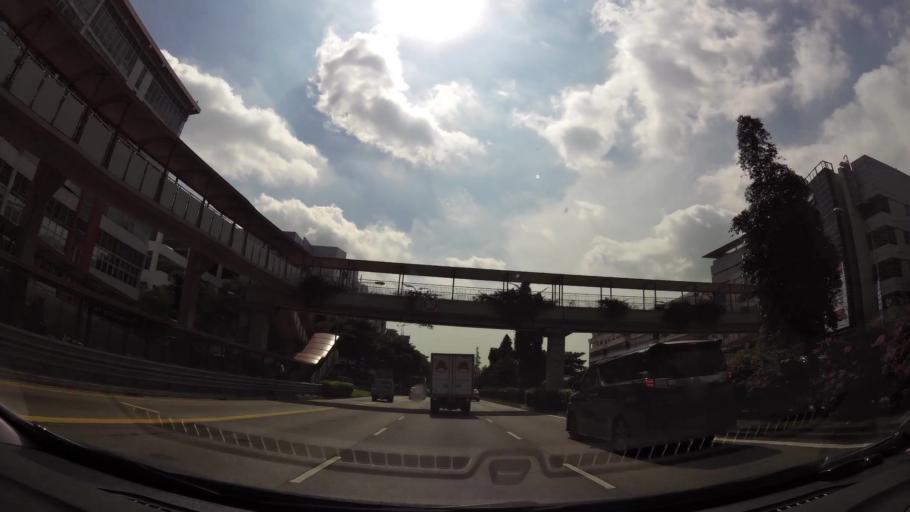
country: SG
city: Singapore
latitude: 1.3334
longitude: 103.9008
